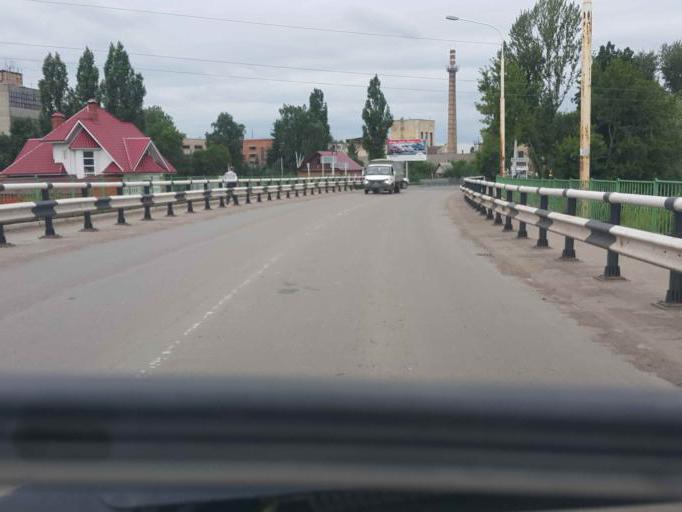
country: RU
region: Tambov
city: Zavoronezhskoye
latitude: 52.8814
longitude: 40.5308
